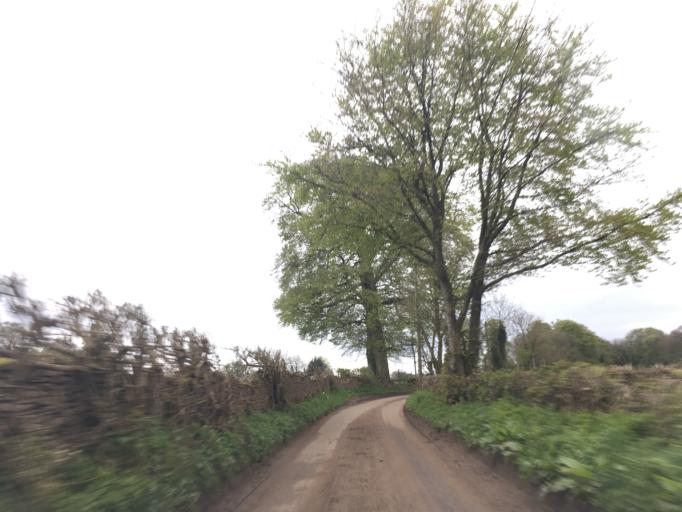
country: GB
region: England
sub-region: Gloucestershire
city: Wotton-under-Edge
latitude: 51.6420
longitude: -2.3163
